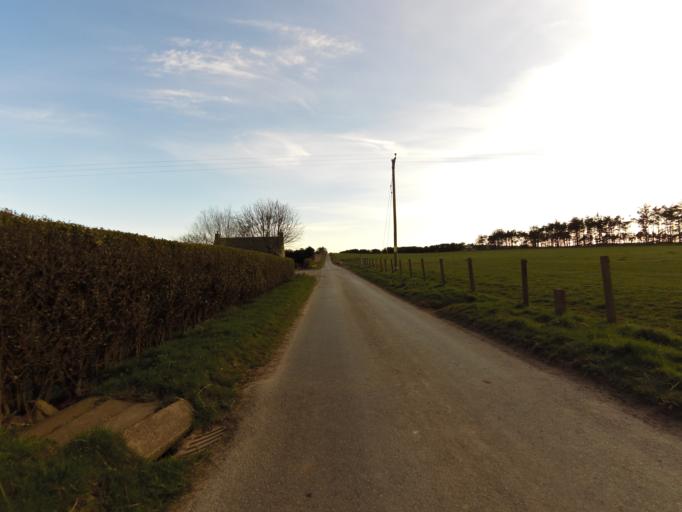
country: GB
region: Scotland
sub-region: Aberdeenshire
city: Stonehaven
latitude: 56.9430
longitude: -2.2206
